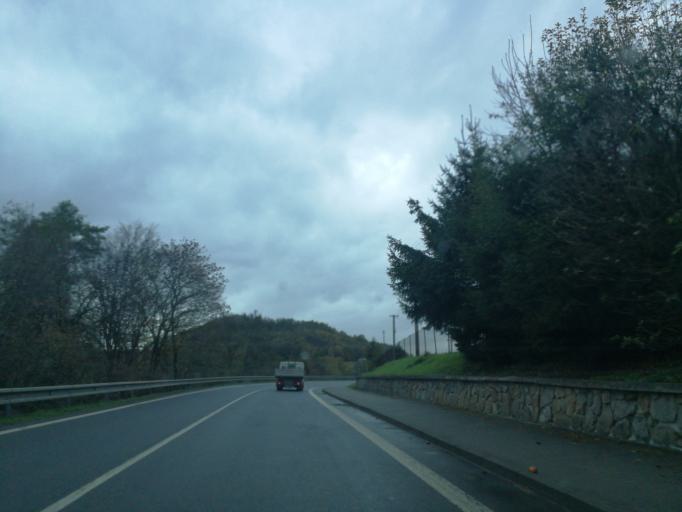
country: CZ
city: Hodslavice
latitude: 49.5296
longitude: 18.0176
